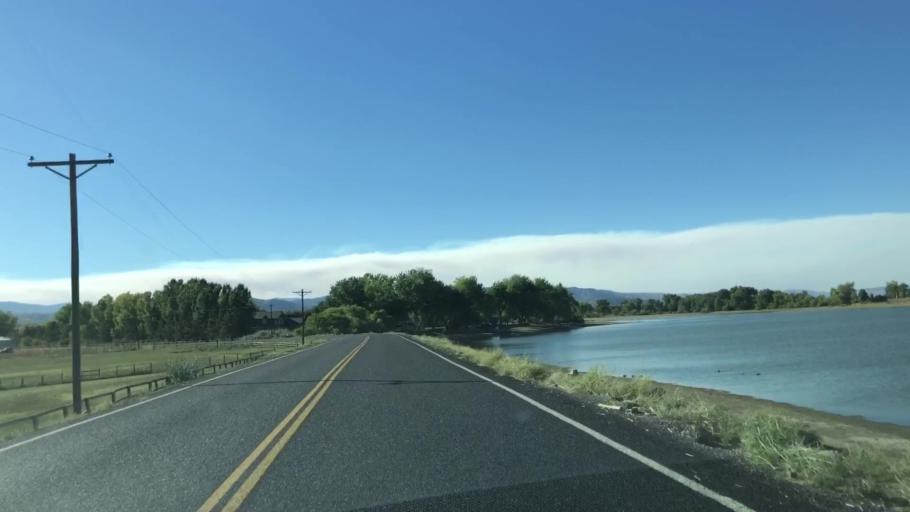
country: US
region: Colorado
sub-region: Larimer County
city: Loveland
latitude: 40.4613
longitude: -105.0540
